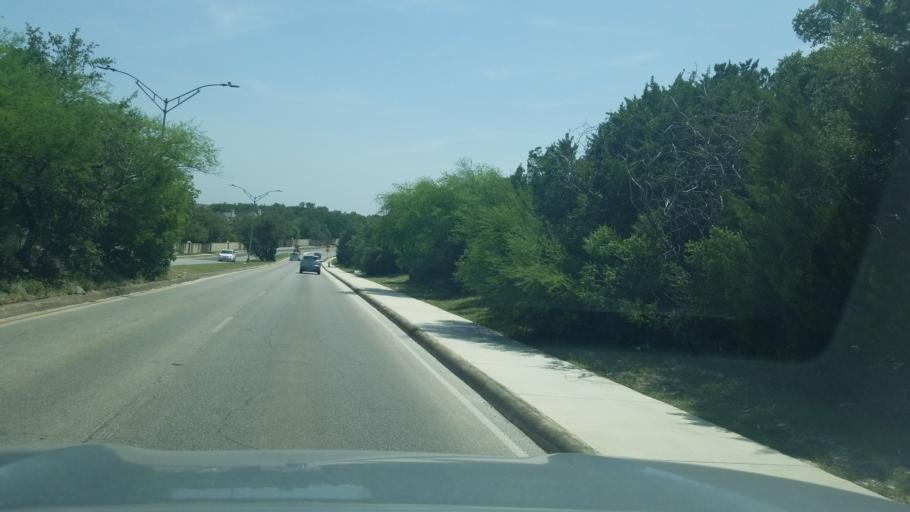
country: US
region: Texas
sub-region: Bexar County
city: Hollywood Park
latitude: 29.6176
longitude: -98.5168
